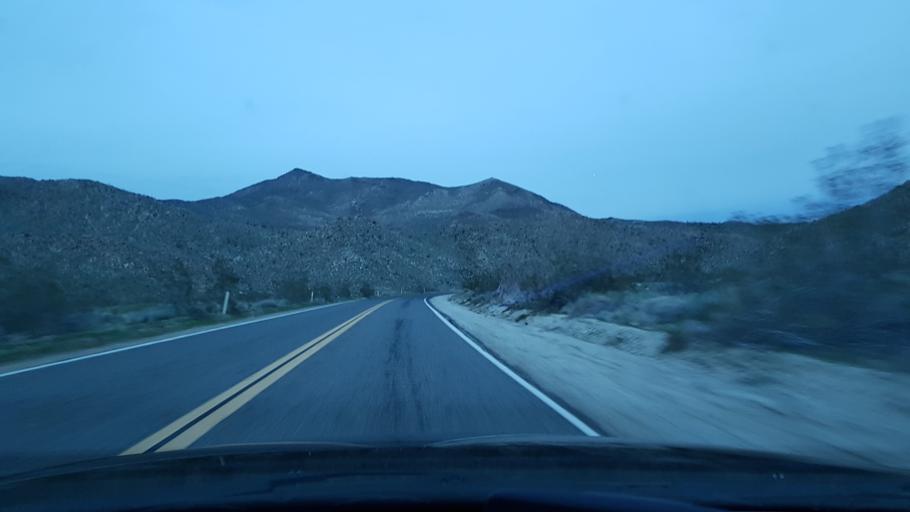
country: US
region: California
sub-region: San Diego County
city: Julian
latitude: 33.0094
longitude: -116.4562
